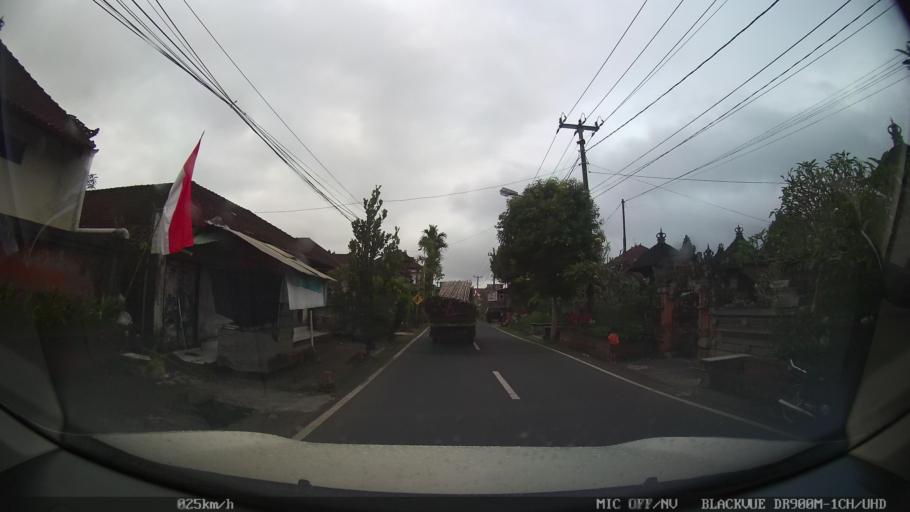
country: ID
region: Bali
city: Badung
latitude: -8.4266
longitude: 115.2463
